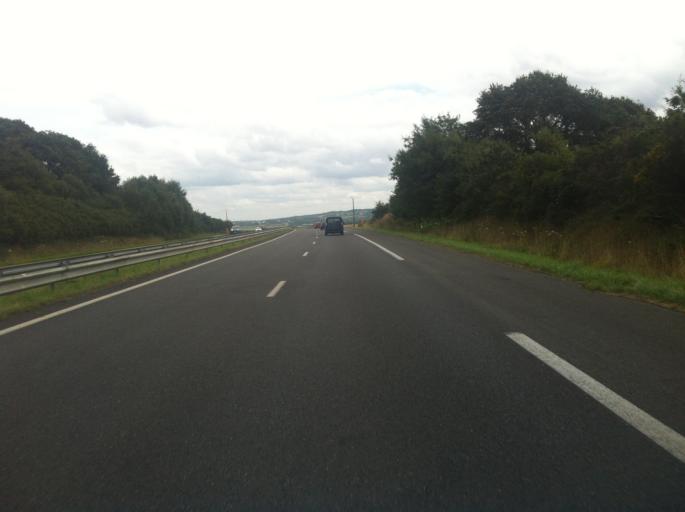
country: FR
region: Brittany
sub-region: Departement du Finistere
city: Plouigneau
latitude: 48.5717
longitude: -3.6791
